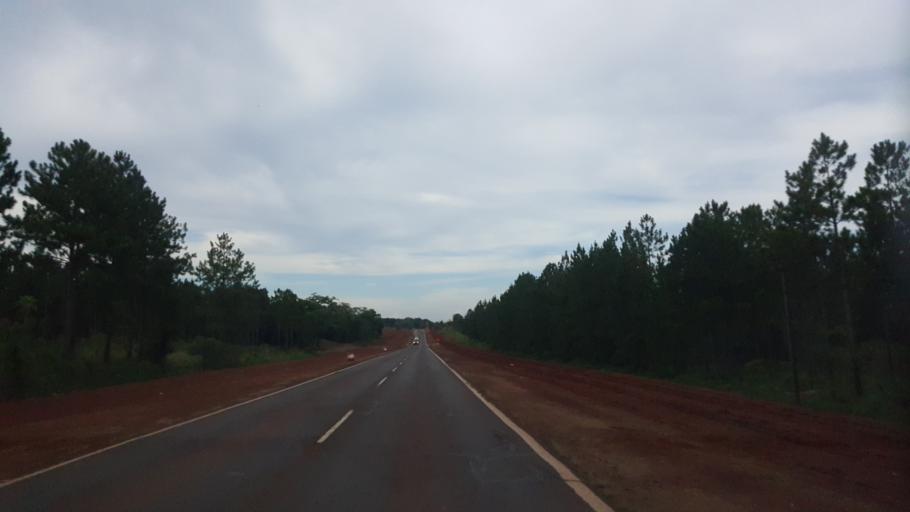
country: AR
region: Misiones
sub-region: Departamento de Candelaria
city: Loreto
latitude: -27.3442
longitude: -55.5464
